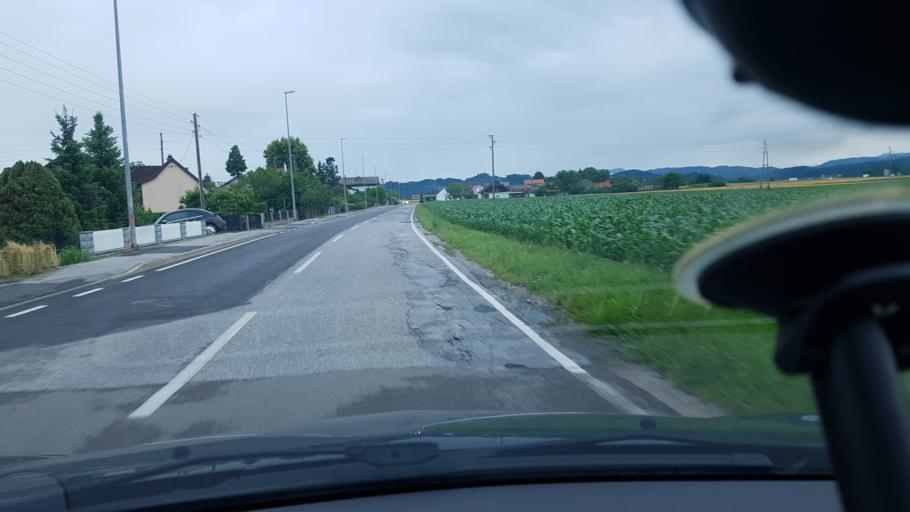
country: SI
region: Hajdina
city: Spodnja Hajdina
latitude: 46.3929
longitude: 15.8669
